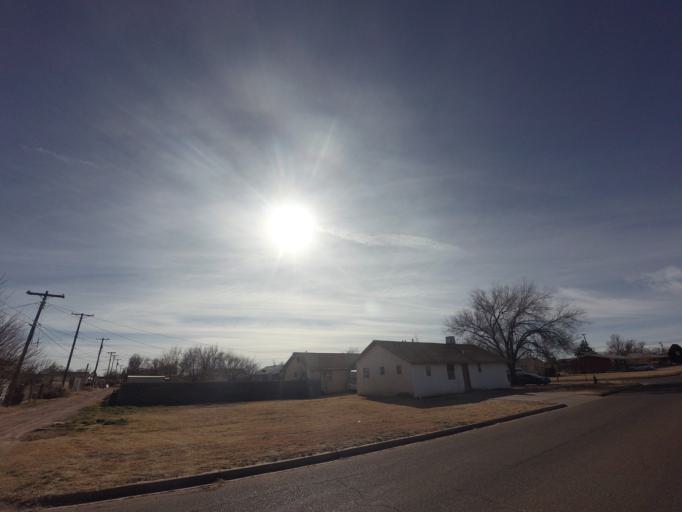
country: US
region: New Mexico
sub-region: Curry County
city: Clovis
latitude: 34.4078
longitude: -103.2212
